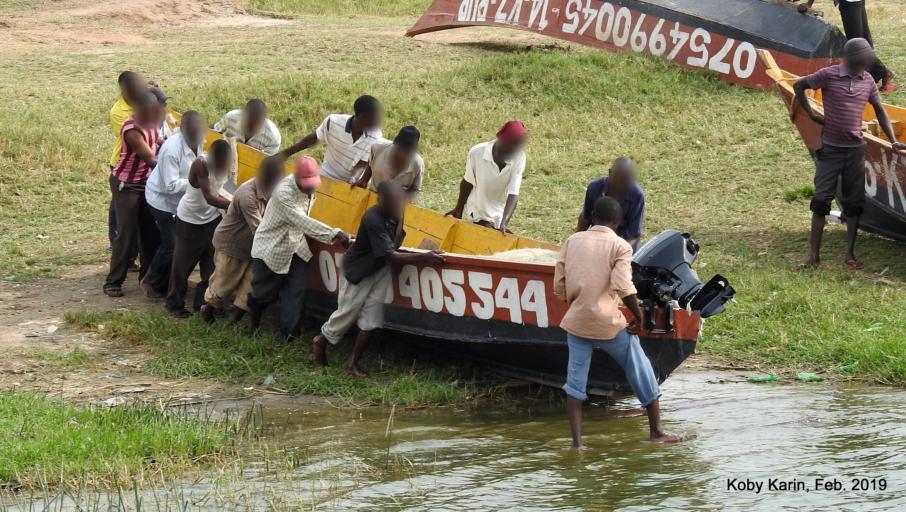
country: UG
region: Western Region
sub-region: Rubirizi District
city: Rubirizi
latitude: -0.2071
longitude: 29.8930
